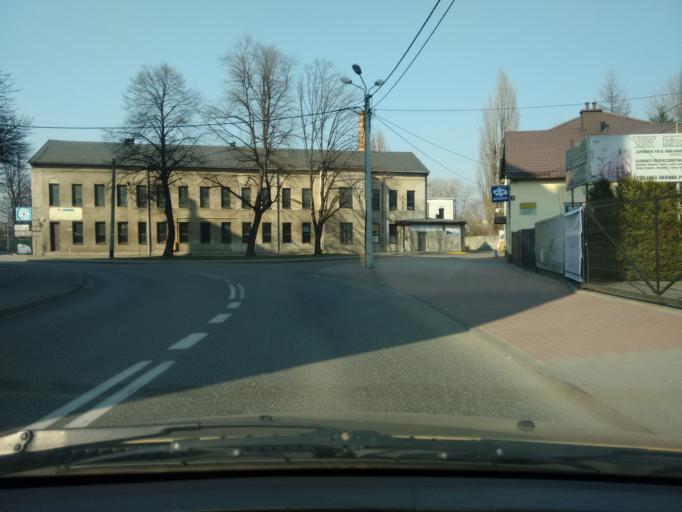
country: PL
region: Silesian Voivodeship
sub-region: Bielsko-Biala
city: Bielsko-Biala
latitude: 49.8364
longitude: 19.0493
